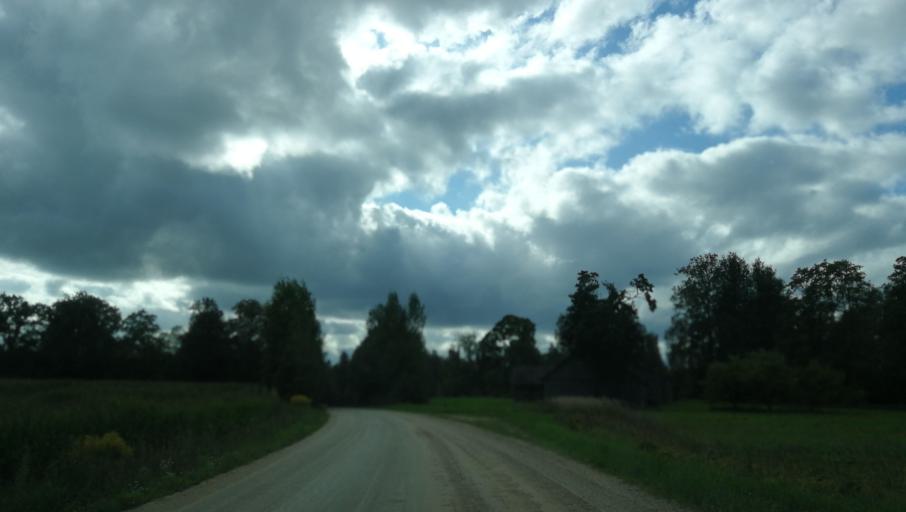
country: LV
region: Malpils
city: Malpils
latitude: 56.9641
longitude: 24.9871
